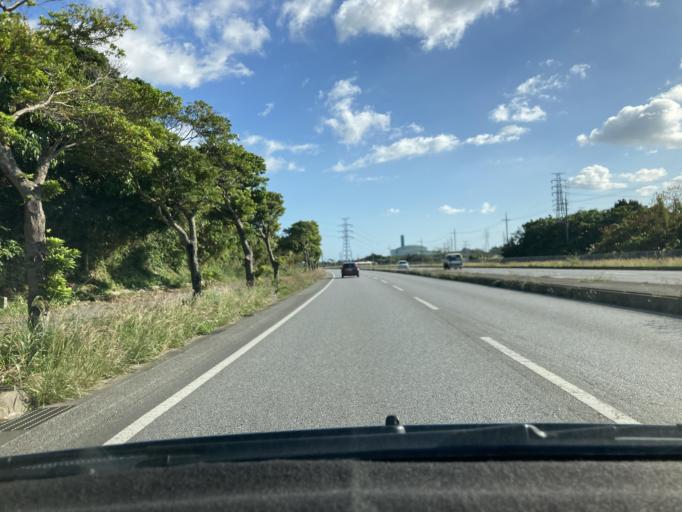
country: JP
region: Okinawa
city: Ishikawa
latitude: 26.4077
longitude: 127.8208
